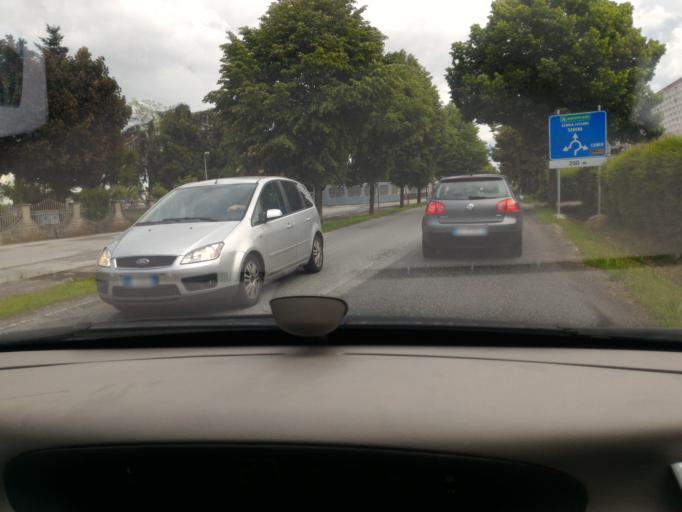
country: IT
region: Piedmont
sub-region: Provincia di Cuneo
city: Genola
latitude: 44.5950
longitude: 7.6592
